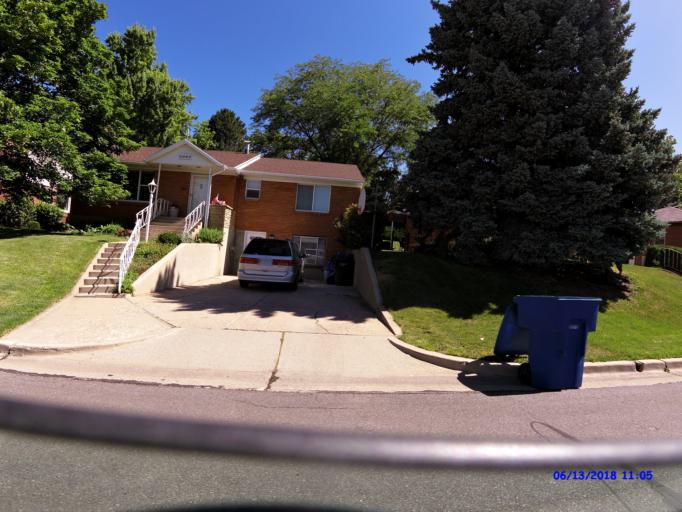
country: US
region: Utah
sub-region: Weber County
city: South Ogden
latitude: 41.2082
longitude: -111.9431
